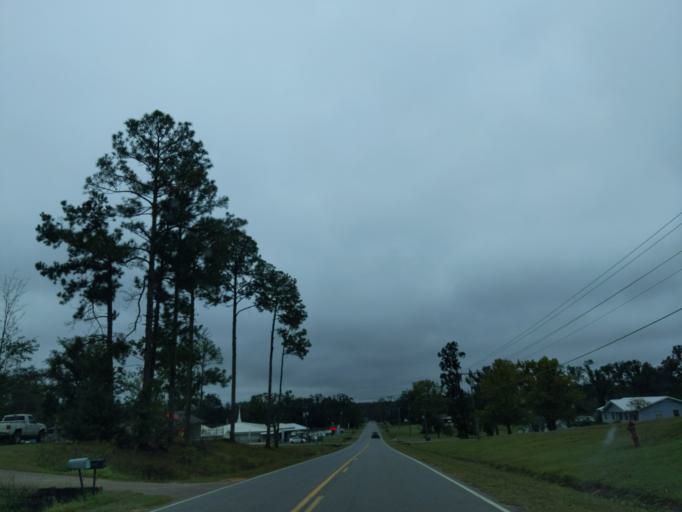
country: US
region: Florida
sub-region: Jackson County
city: Sneads
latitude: 30.7147
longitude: -84.9325
